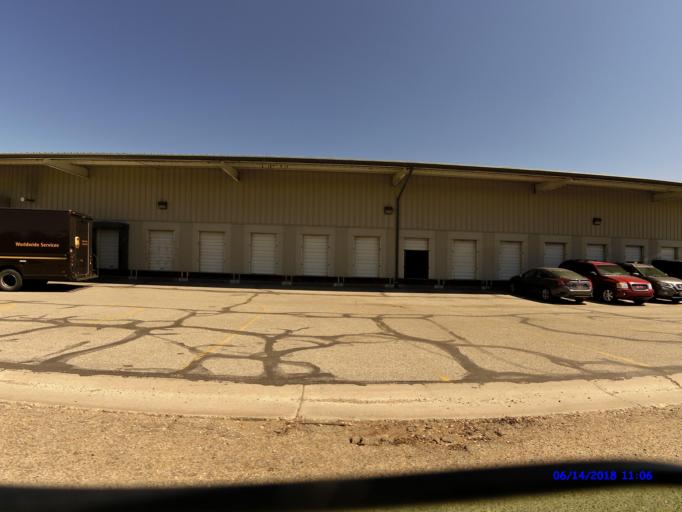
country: US
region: Utah
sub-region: Weber County
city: Ogden
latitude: 41.2149
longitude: -112.0047
